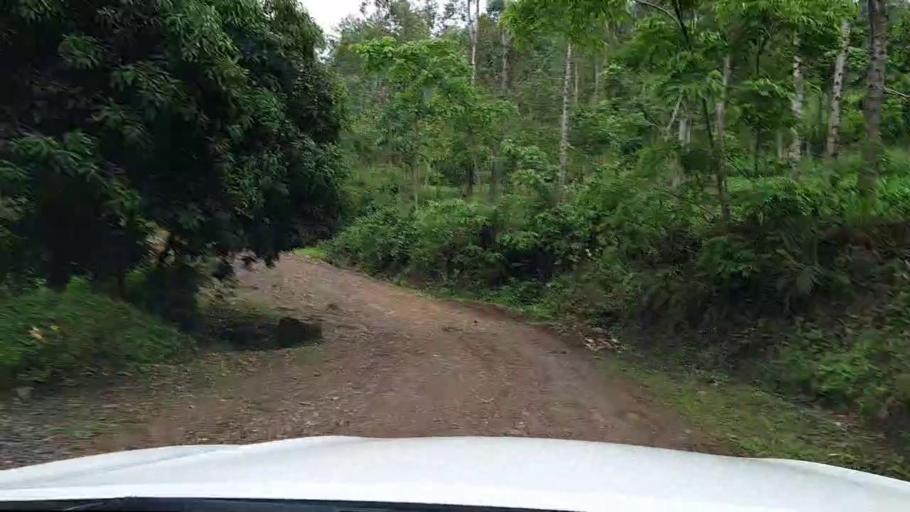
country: RW
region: Western Province
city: Cyangugu
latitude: -2.5582
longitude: 29.0355
